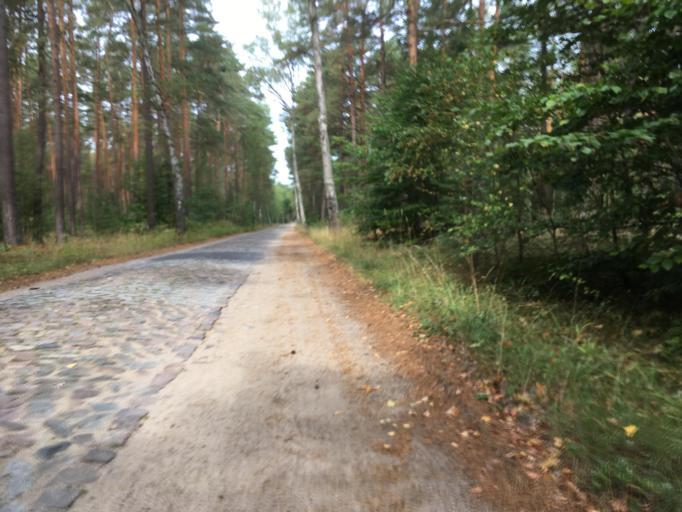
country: DE
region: Brandenburg
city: Milmersdorf
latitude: 53.0522
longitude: 13.6341
